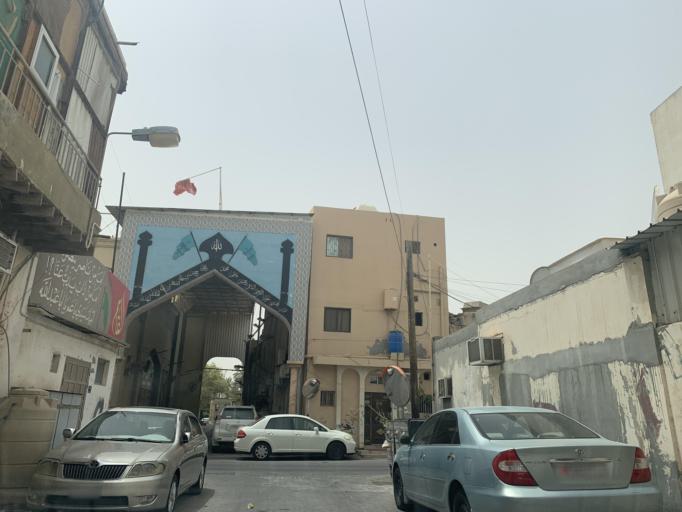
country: BH
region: Manama
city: Jidd Hafs
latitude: 26.2305
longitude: 50.5278
